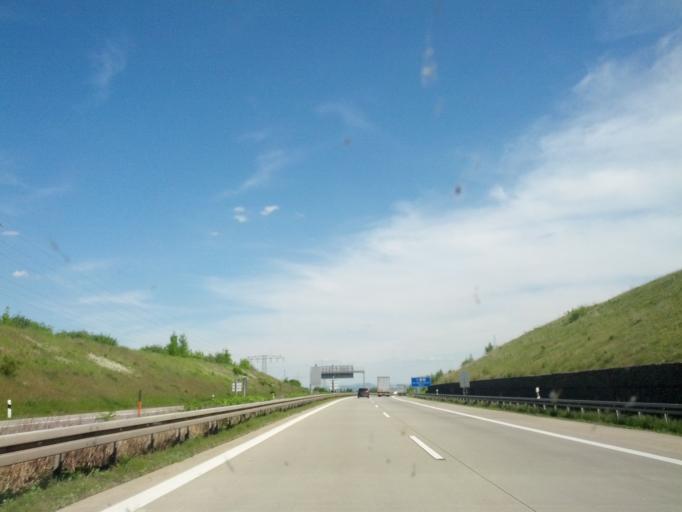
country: DE
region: Saxony
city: Bannewitz
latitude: 51.0073
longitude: 13.7328
